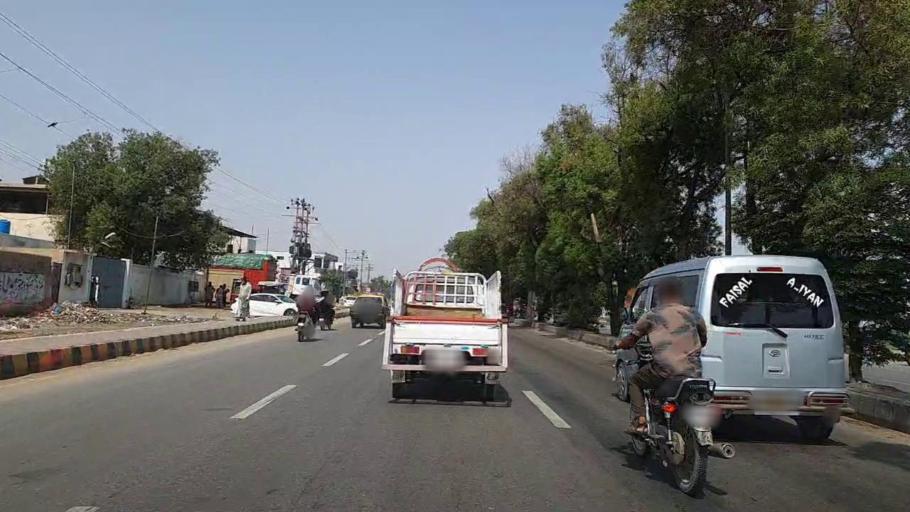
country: PK
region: Sindh
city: Malir Cantonment
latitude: 24.8554
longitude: 67.2553
